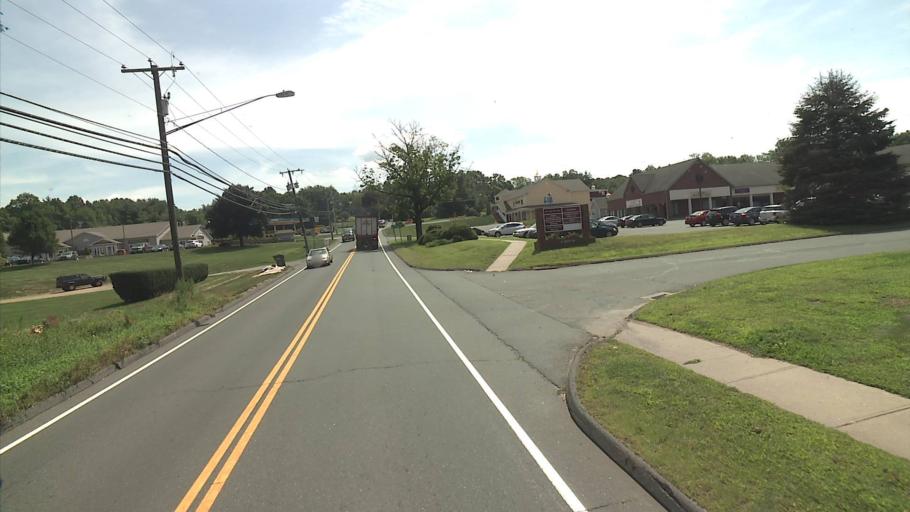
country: US
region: Connecticut
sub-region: Tolland County
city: Ellington
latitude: 41.9012
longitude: -72.4612
